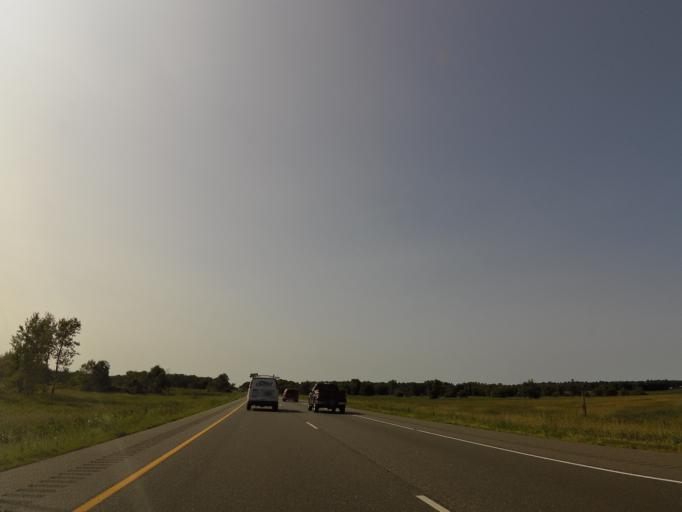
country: US
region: Wisconsin
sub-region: Juneau County
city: New Lisbon
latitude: 43.9487
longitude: -90.3270
